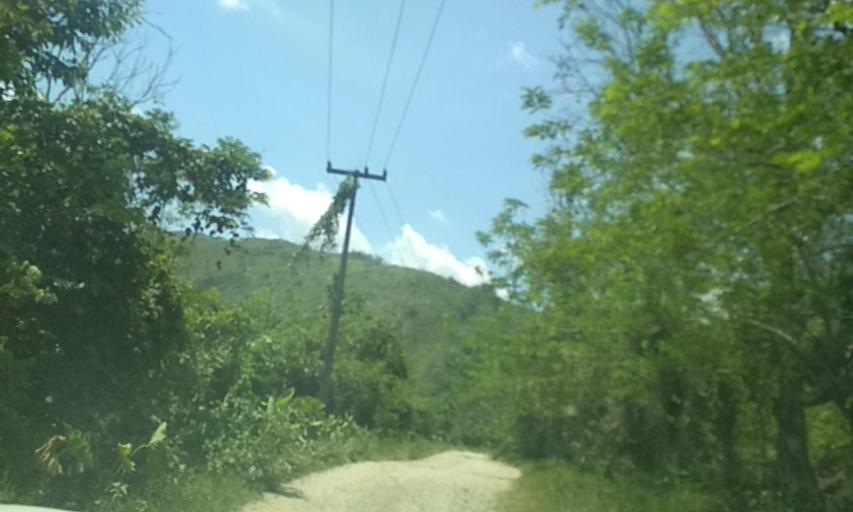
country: MX
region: Chiapas
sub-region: Tecpatan
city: Raudales Malpaso
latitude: 17.2899
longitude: -93.8426
